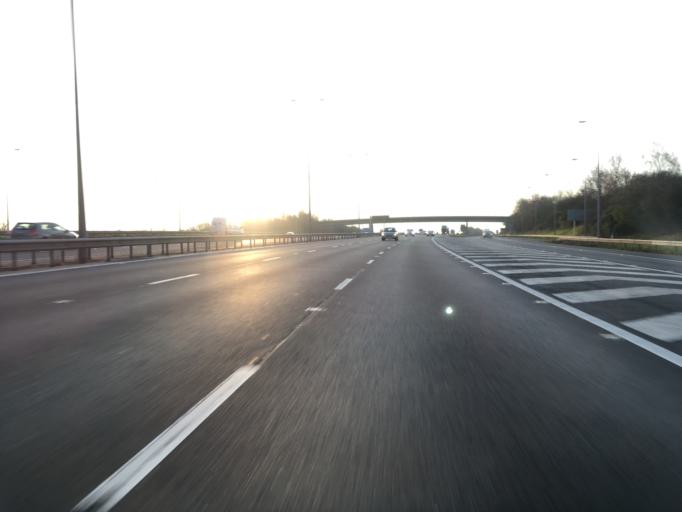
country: GB
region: England
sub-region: Worcestershire
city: Bredon
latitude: 52.0546
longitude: -2.1398
